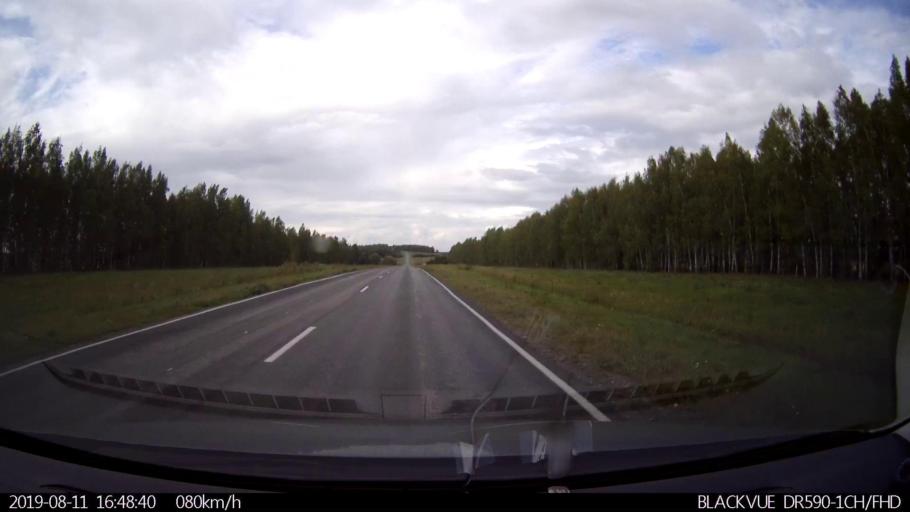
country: RU
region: Ulyanovsk
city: Mayna
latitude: 54.2113
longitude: 47.6930
